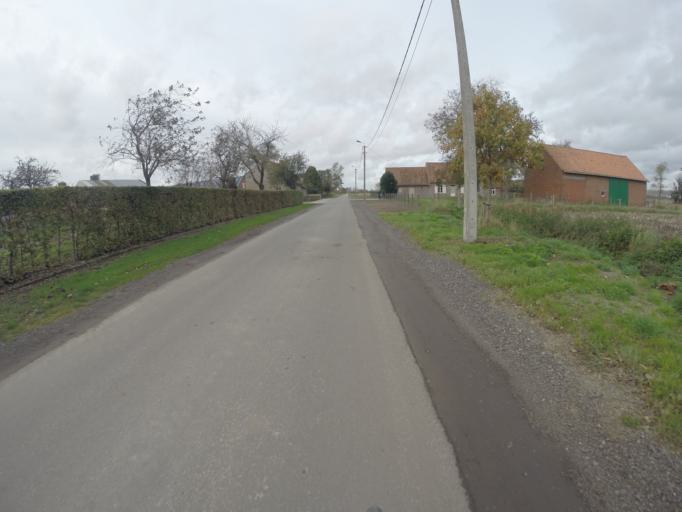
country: BE
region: Flanders
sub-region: Provincie Oost-Vlaanderen
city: Knesselare
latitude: 51.1572
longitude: 3.4020
